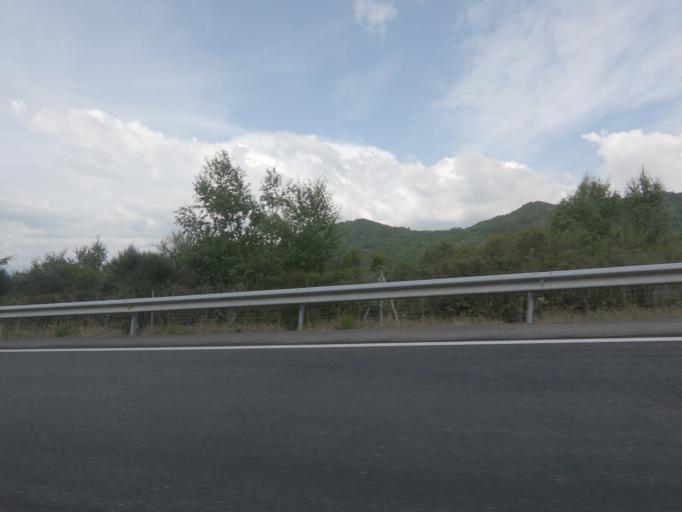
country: ES
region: Galicia
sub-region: Provincia de Ourense
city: Ambia
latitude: 42.1776
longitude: -7.7636
